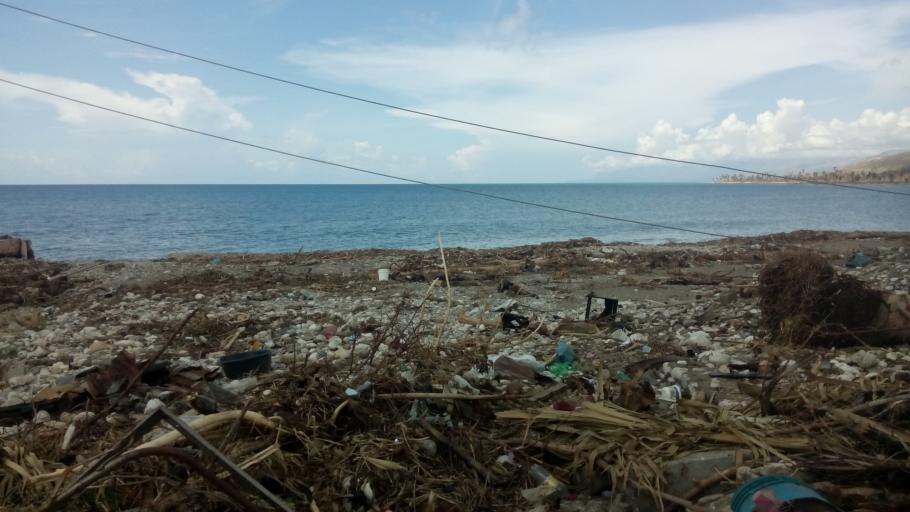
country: HT
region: Sud
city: Roche-a-Bateau
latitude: 18.1783
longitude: -74.0036
